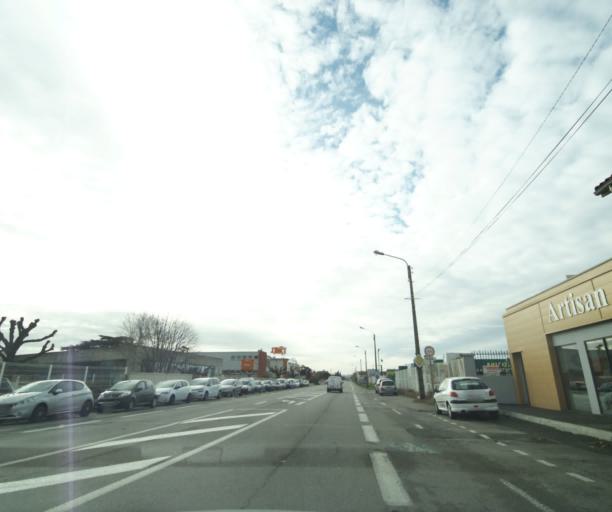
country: FR
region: Rhone-Alpes
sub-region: Departement de la Drome
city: Bourg-les-Valence
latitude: 44.9580
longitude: 4.8893
